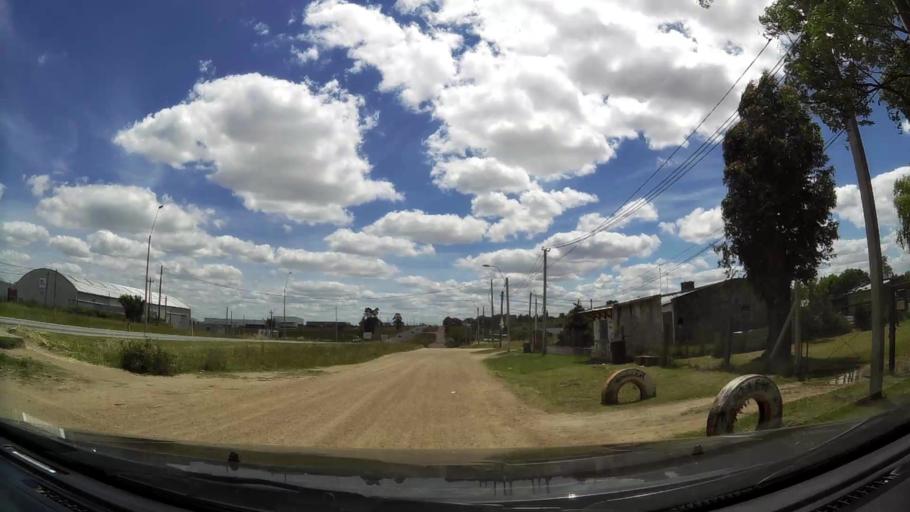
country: UY
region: Canelones
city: Colonia Nicolich
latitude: -34.7943
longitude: -56.0025
